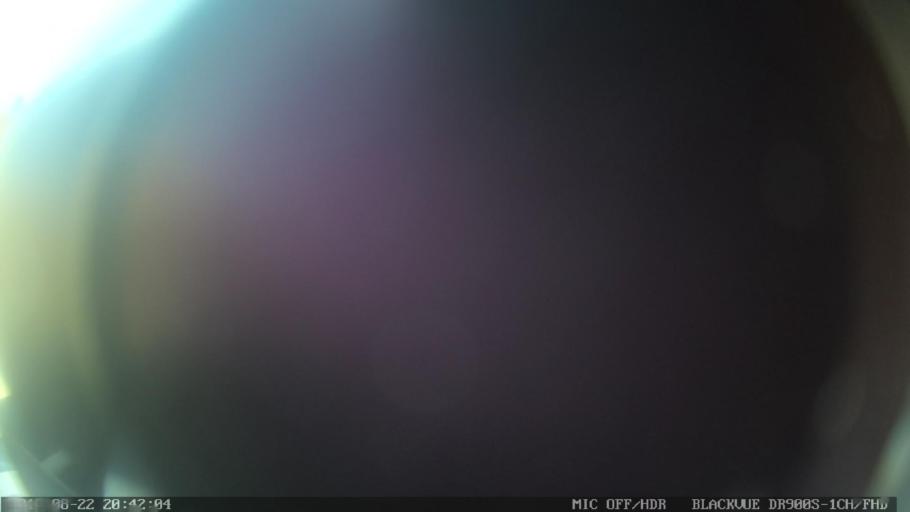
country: PT
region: Castelo Branco
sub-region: Proenca-A-Nova
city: Proenca-a-Nova
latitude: 39.6915
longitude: -7.8116
